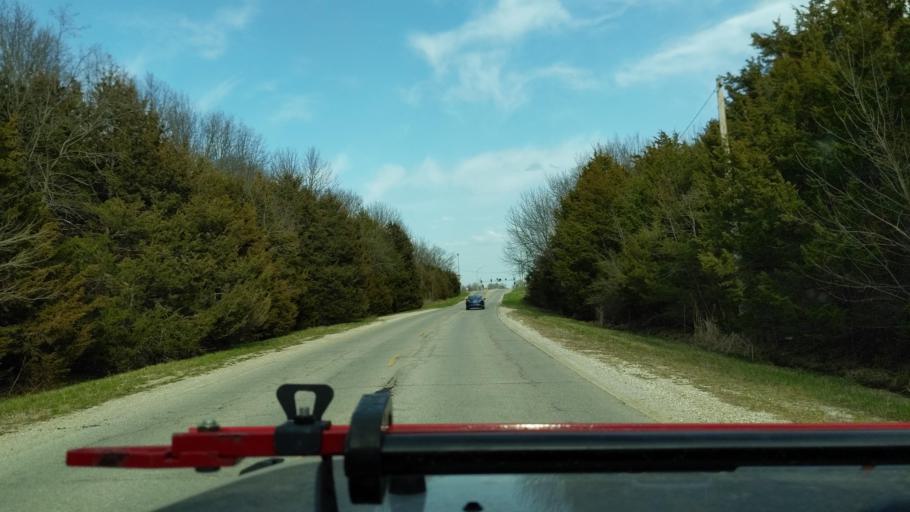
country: US
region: Missouri
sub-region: Macon County
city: Macon
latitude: 39.7521
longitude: -92.4718
